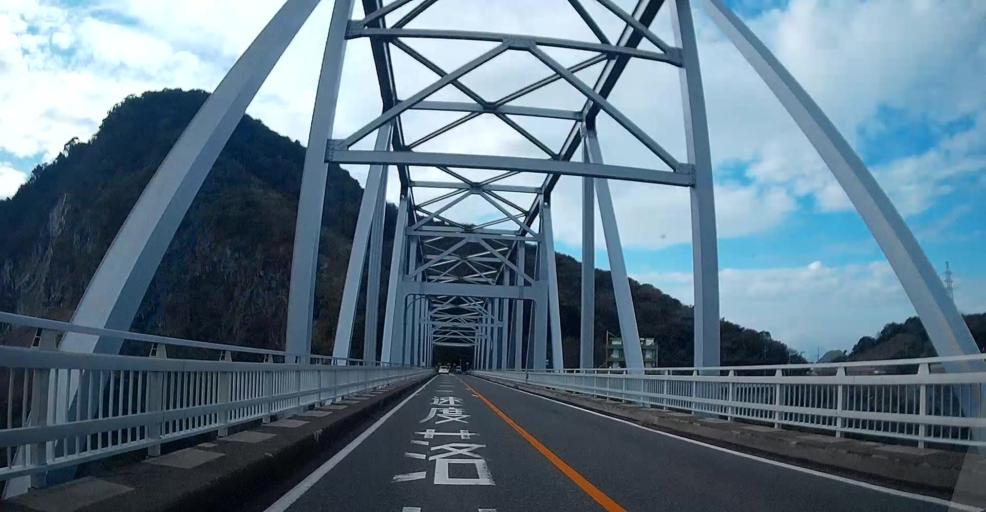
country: JP
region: Kumamoto
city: Yatsushiro
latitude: 32.6114
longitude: 130.4577
